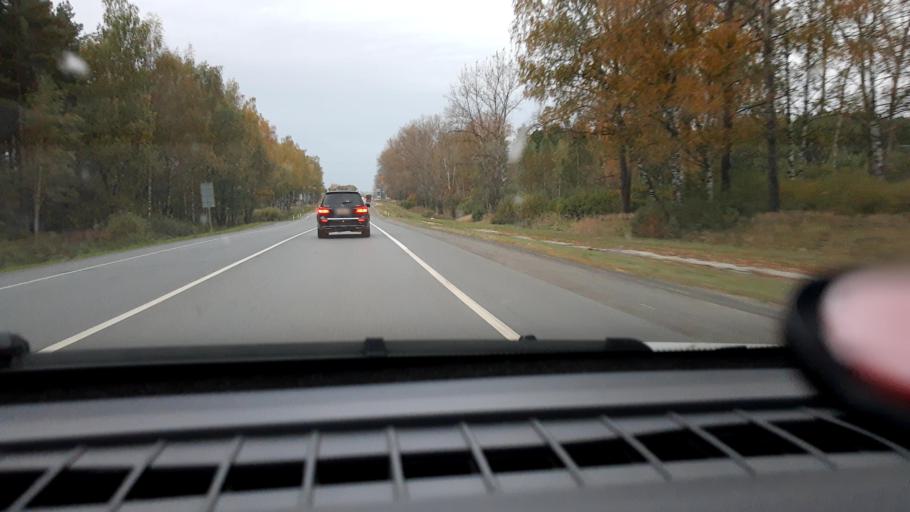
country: RU
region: Vladimir
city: Orgtrud
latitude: 56.2100
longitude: 40.6053
